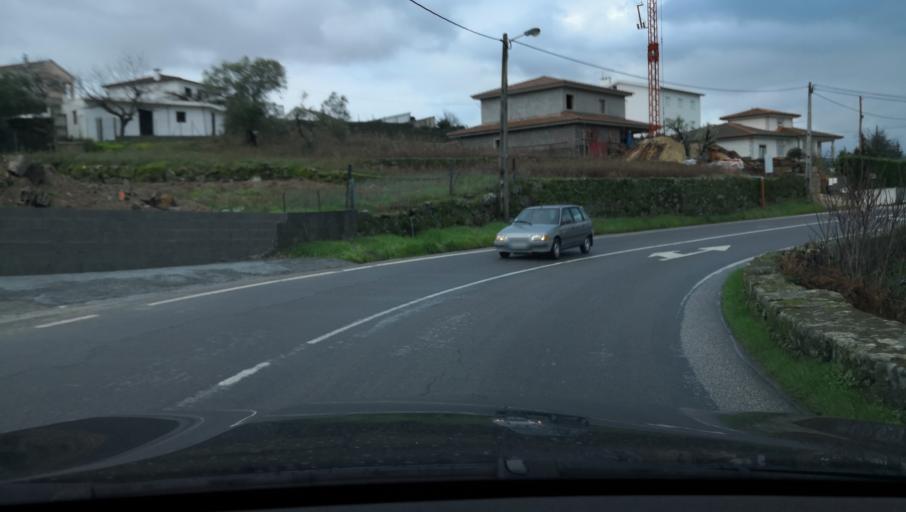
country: PT
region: Vila Real
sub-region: Vila Real
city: Vila Real
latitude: 41.3305
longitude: -7.7291
